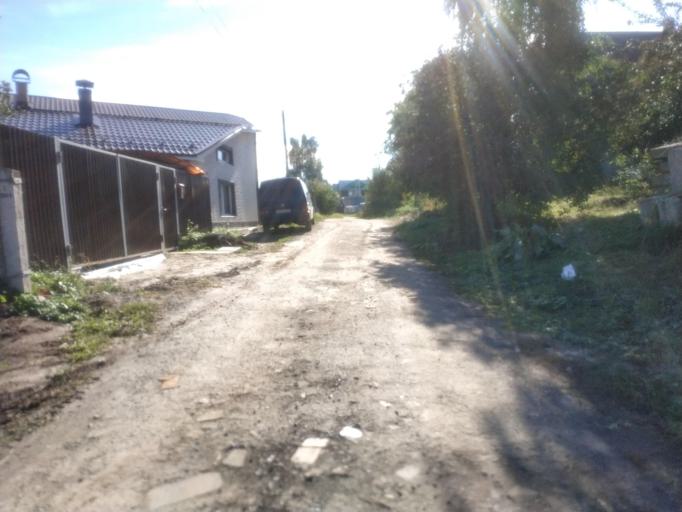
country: RU
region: Chuvashia
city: Novyye Lapsary
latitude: 56.1468
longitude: 47.1505
